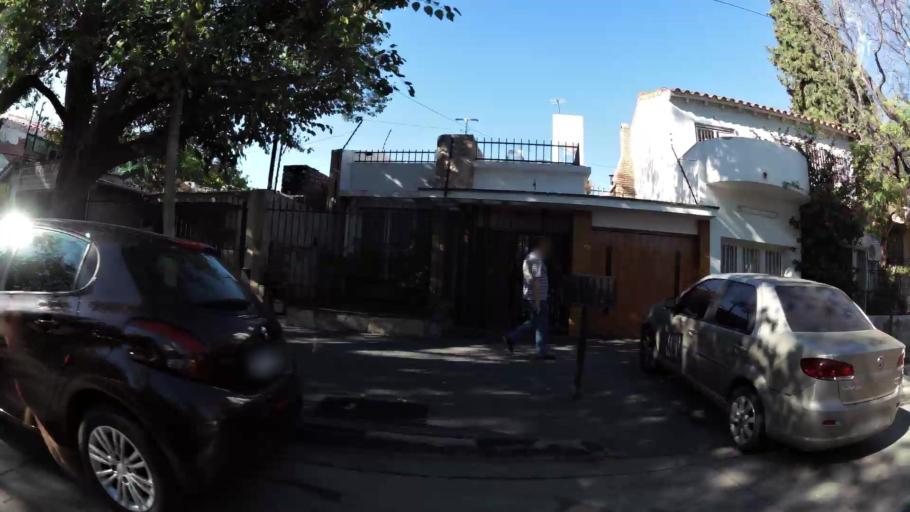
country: AR
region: Mendoza
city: Las Heras
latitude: -32.8689
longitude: -68.8519
